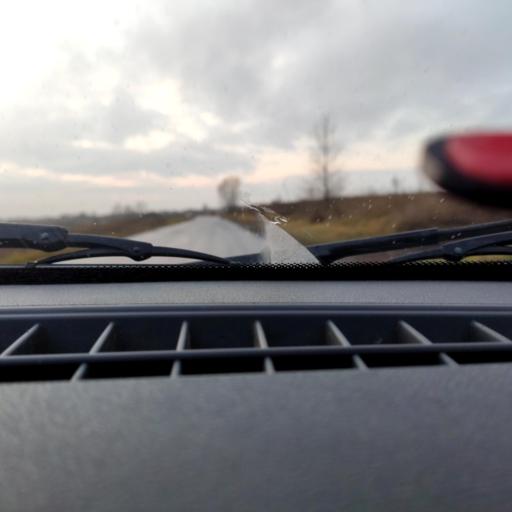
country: RU
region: Bashkortostan
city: Avdon
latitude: 54.5111
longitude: 55.8512
